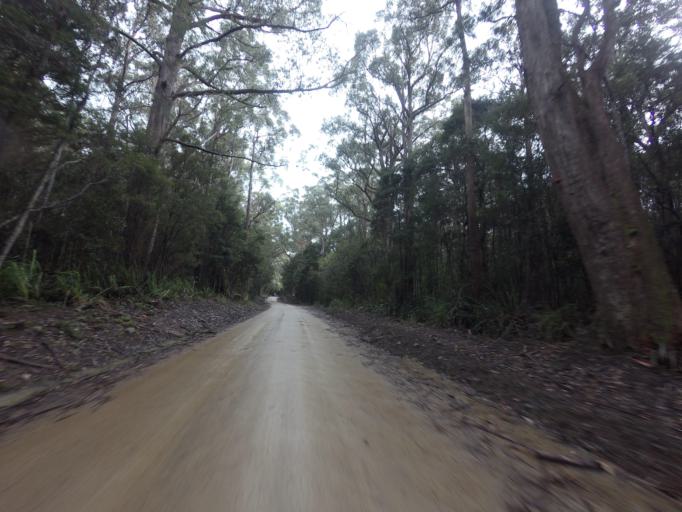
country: AU
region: Tasmania
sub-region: Huon Valley
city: Geeveston
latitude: -43.5594
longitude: 146.8907
